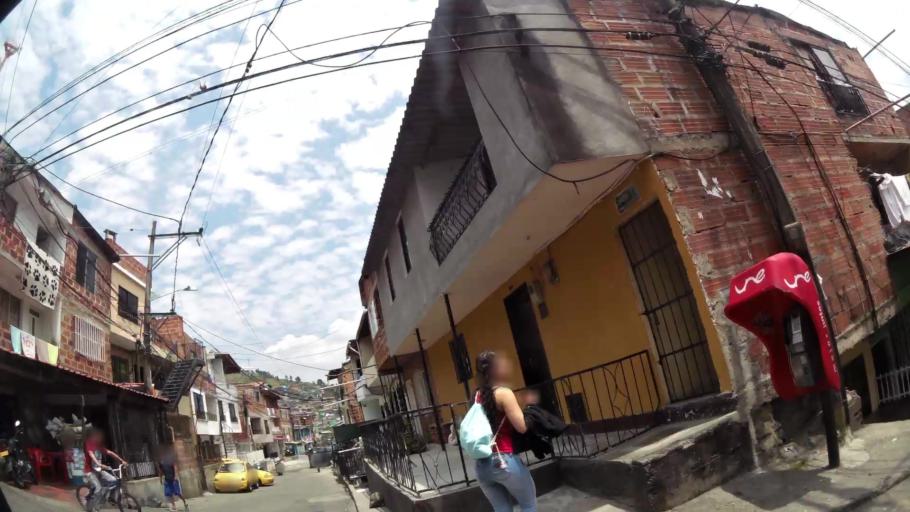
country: CO
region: Antioquia
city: Bello
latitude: 6.3145
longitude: -75.5825
